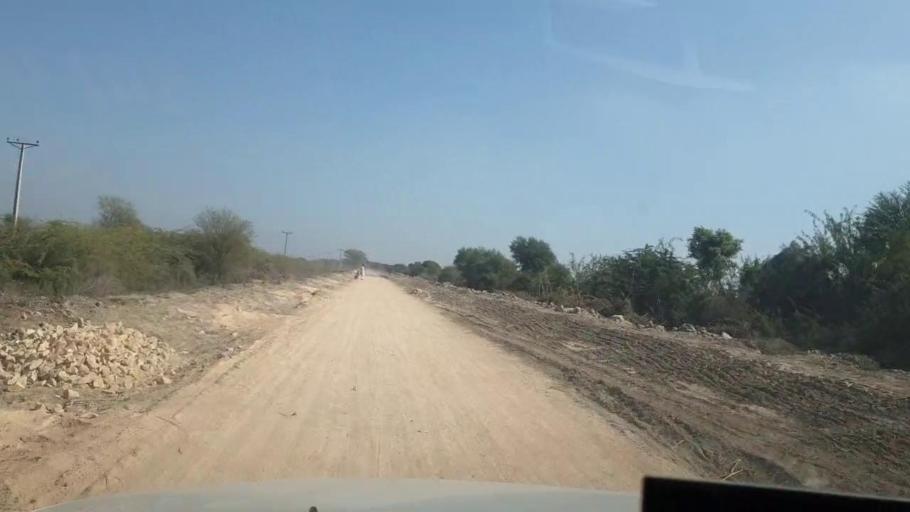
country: PK
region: Sindh
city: Kotri
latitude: 25.1621
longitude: 68.3010
